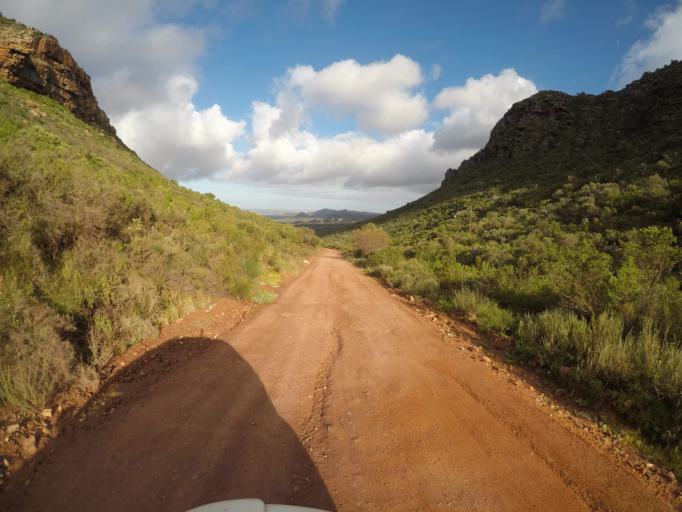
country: ZA
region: Western Cape
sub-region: West Coast District Municipality
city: Clanwilliam
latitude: -32.3404
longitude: 18.7876
